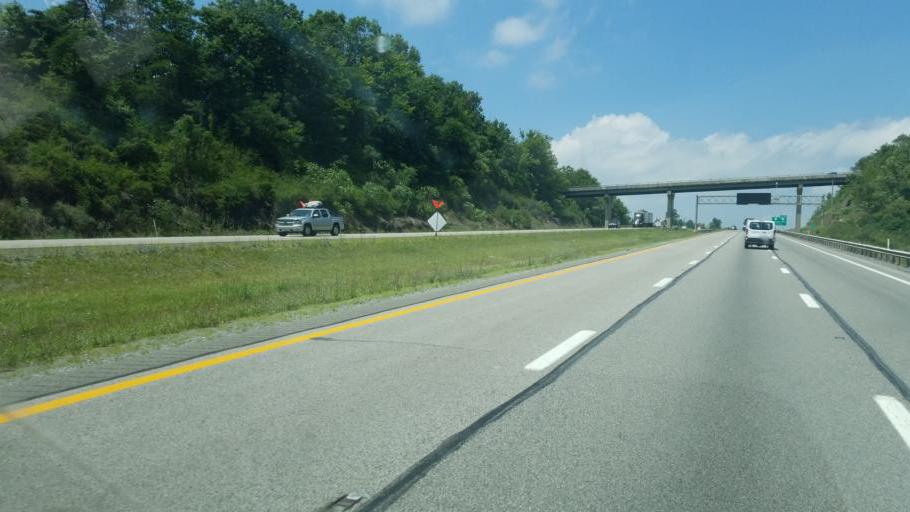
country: US
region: West Virginia
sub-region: Mercer County
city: Princeton
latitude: 37.3925
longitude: -81.0593
